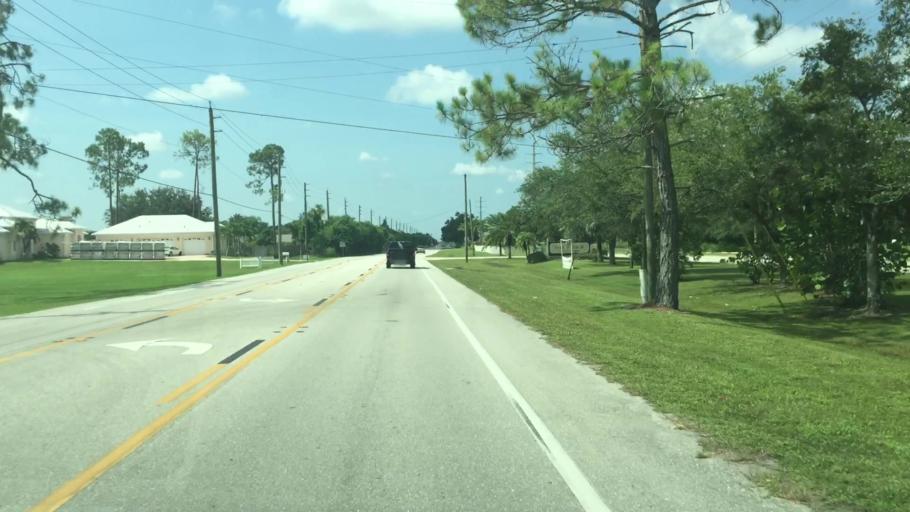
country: US
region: Florida
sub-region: Lee County
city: Villas
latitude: 26.5550
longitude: -81.8467
